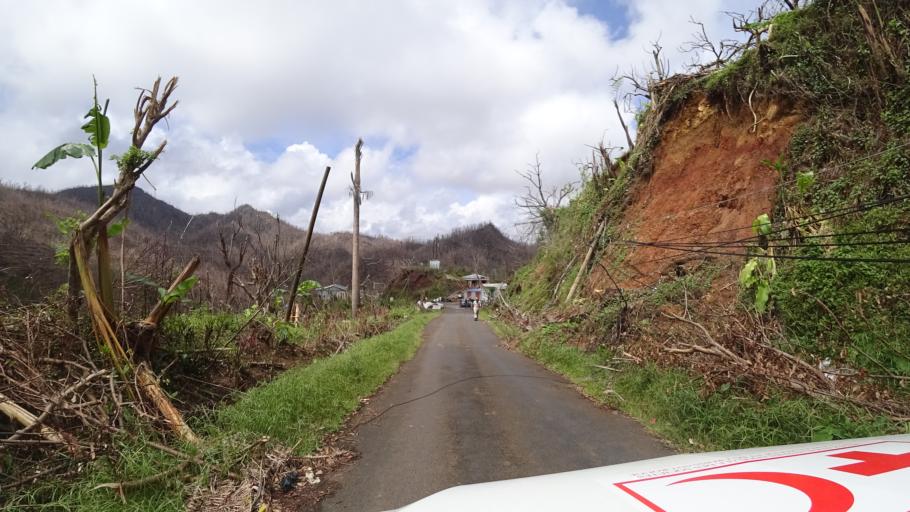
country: DM
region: Saint David
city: Rosalie
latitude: 15.3938
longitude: -61.2598
